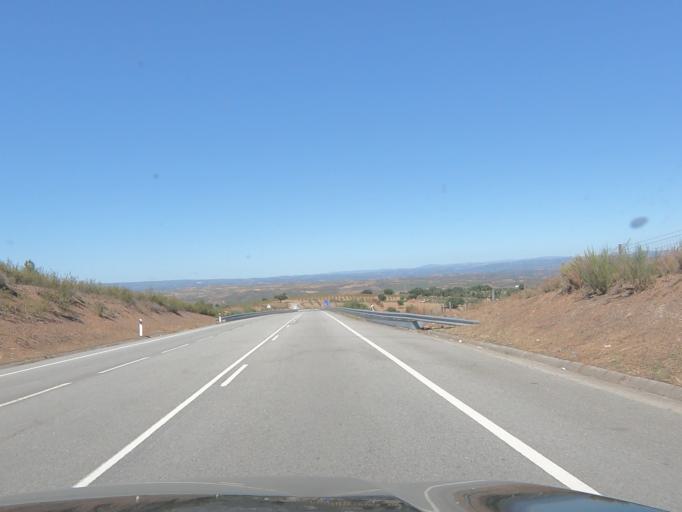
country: PT
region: Braganca
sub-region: Mirandela
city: Mirandela
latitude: 41.4830
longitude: -7.2244
